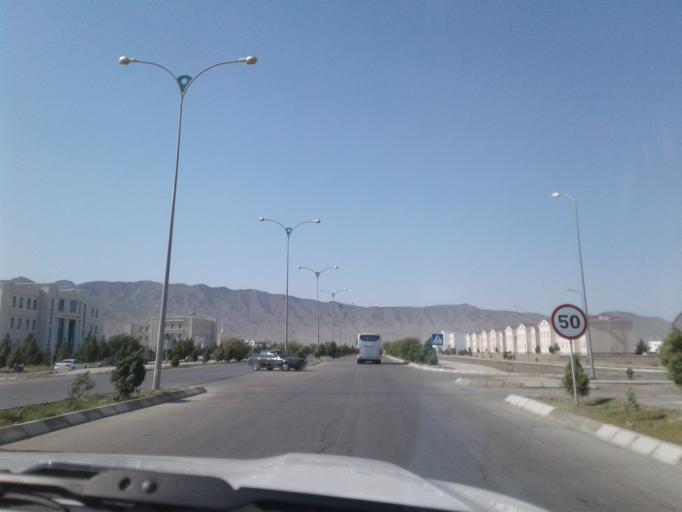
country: TM
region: Balkan
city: Gazanjyk
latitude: 39.2615
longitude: 55.5409
